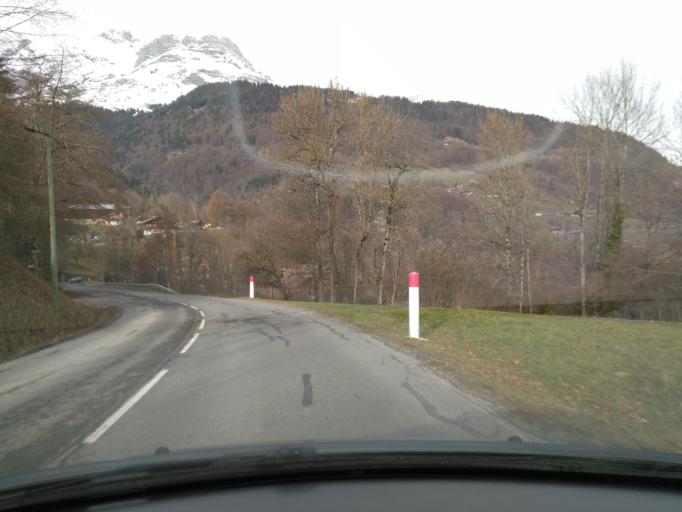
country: FR
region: Rhone-Alpes
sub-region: Departement de la Haute-Savoie
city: Cordon
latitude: 45.9278
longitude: 6.6133
